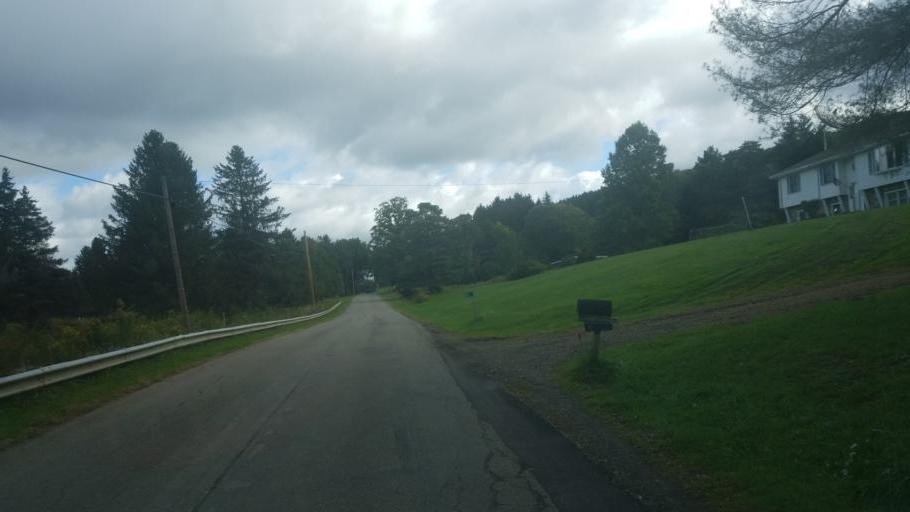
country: US
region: New York
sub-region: Cattaraugus County
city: Weston Mills
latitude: 42.1165
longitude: -78.3142
